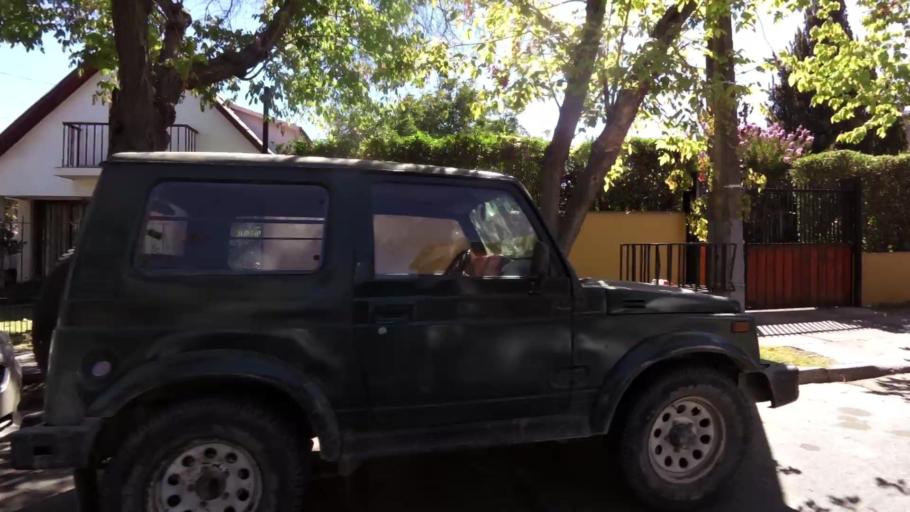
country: CL
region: O'Higgins
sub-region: Provincia de Cachapoal
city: Rancagua
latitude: -34.1754
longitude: -70.7335
